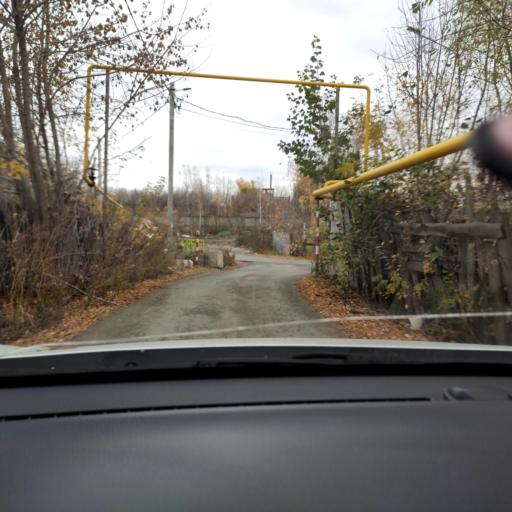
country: RU
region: Tatarstan
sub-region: Gorod Kazan'
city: Kazan
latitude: 55.7520
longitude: 49.1144
